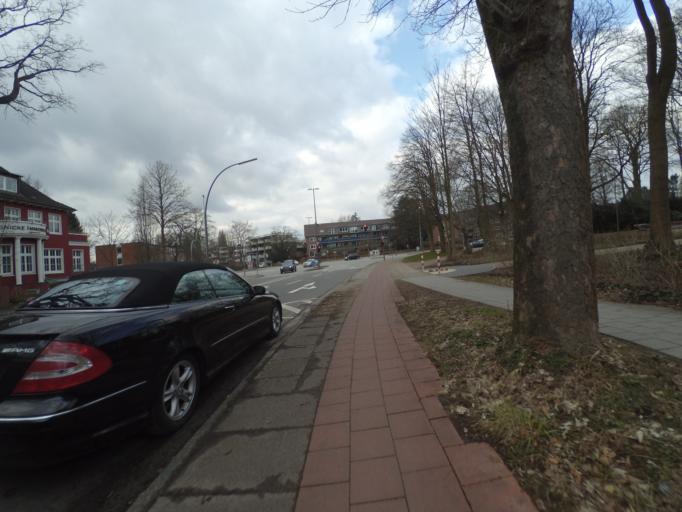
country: DE
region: Hamburg
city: Hamburg-Nord
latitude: 53.5986
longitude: 9.9585
